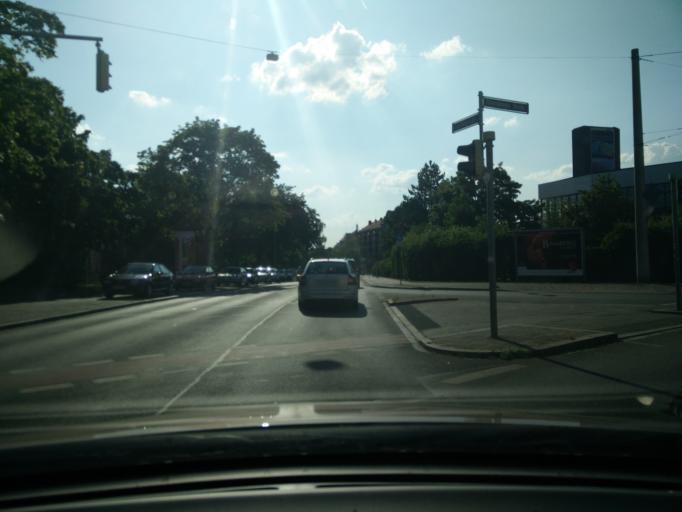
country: DE
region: Bavaria
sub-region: Regierungsbezirk Mittelfranken
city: Nuernberg
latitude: 49.4365
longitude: 11.0914
